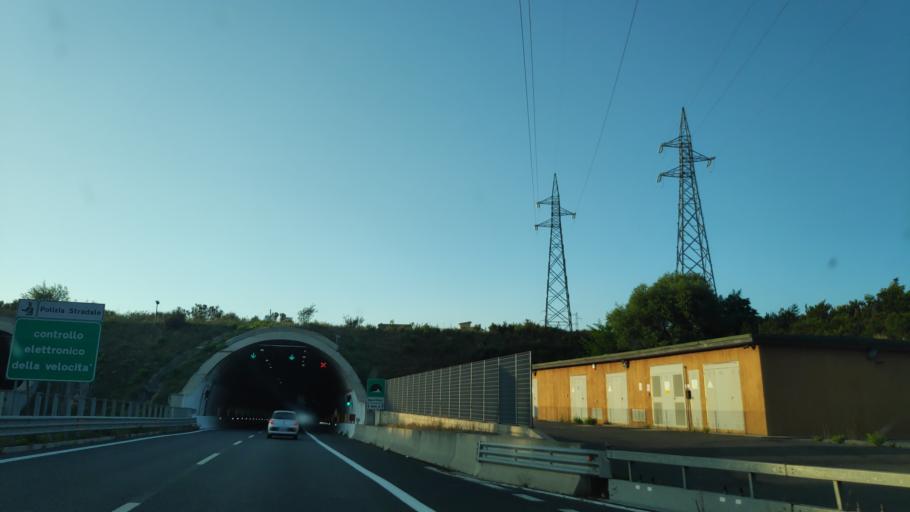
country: IT
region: Calabria
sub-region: Provincia di Reggio Calabria
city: Ceramida-Pellegrina
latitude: 38.3147
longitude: 15.8427
